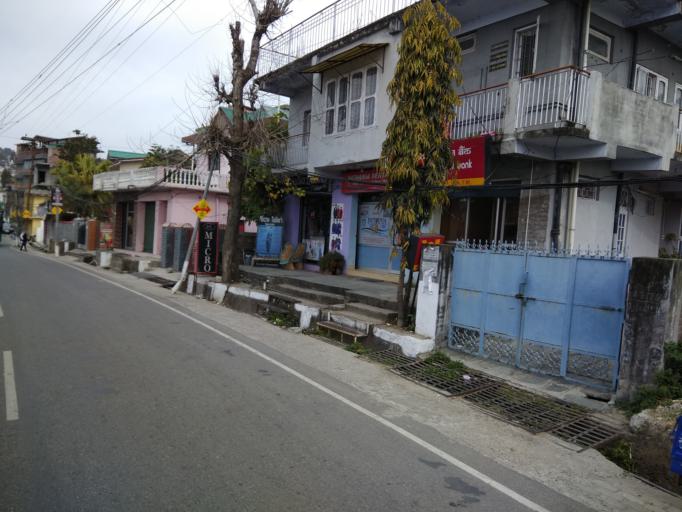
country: IN
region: Himachal Pradesh
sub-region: Kangra
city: Dharmsala
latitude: 32.2029
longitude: 76.3320
